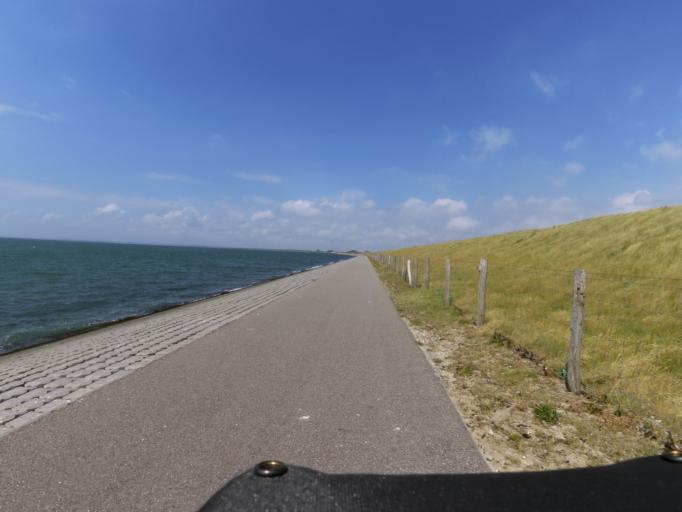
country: NL
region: Zeeland
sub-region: Schouwen-Duiveland
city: Scharendijke
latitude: 51.6701
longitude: 3.8728
